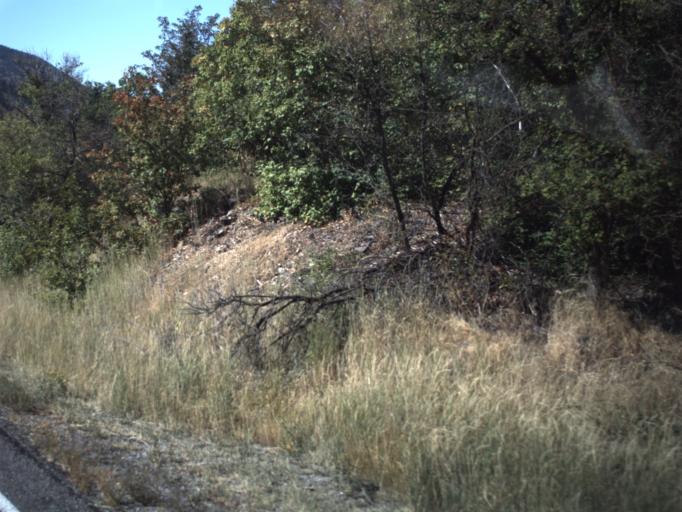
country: US
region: Utah
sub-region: Cache County
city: Millville
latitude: 41.6237
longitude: -111.7323
